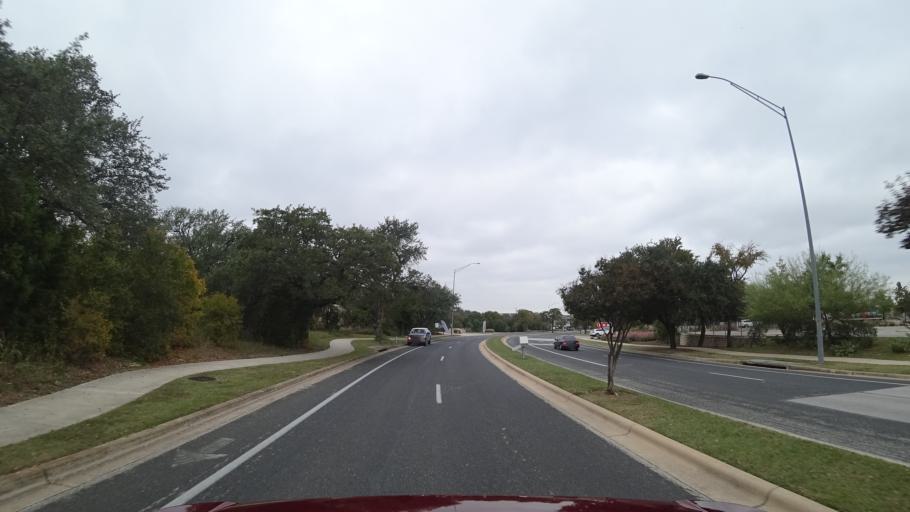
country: US
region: Texas
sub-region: Williamson County
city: Anderson Mill
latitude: 30.4752
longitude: -97.8054
